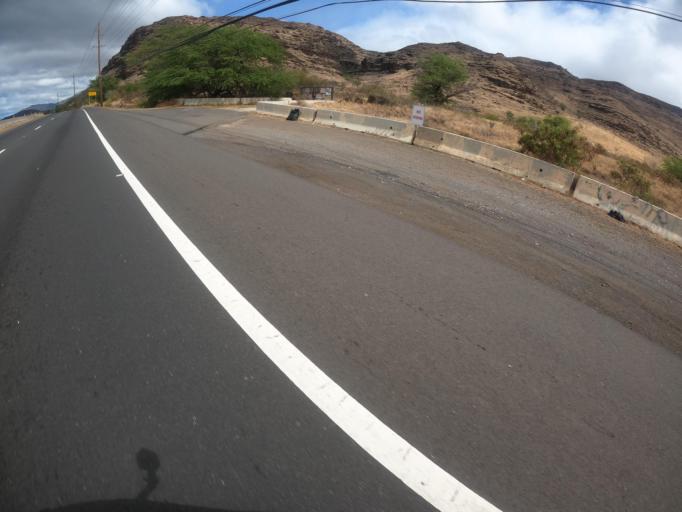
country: US
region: Hawaii
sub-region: Honolulu County
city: Nanakuli
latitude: 21.3608
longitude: -158.1314
